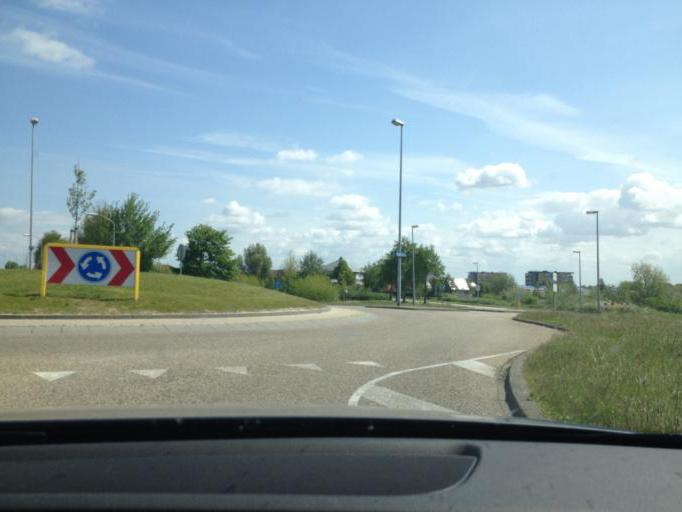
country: NL
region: Flevoland
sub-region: Gemeente Lelystad
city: Lelystad
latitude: 52.4963
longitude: 5.4059
